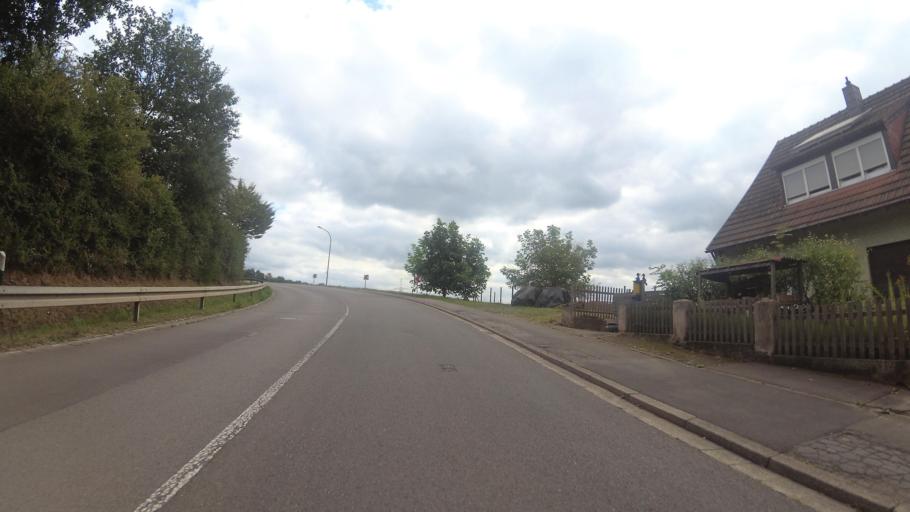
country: DE
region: Saarland
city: Puttlingen
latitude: 49.2595
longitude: 6.8942
